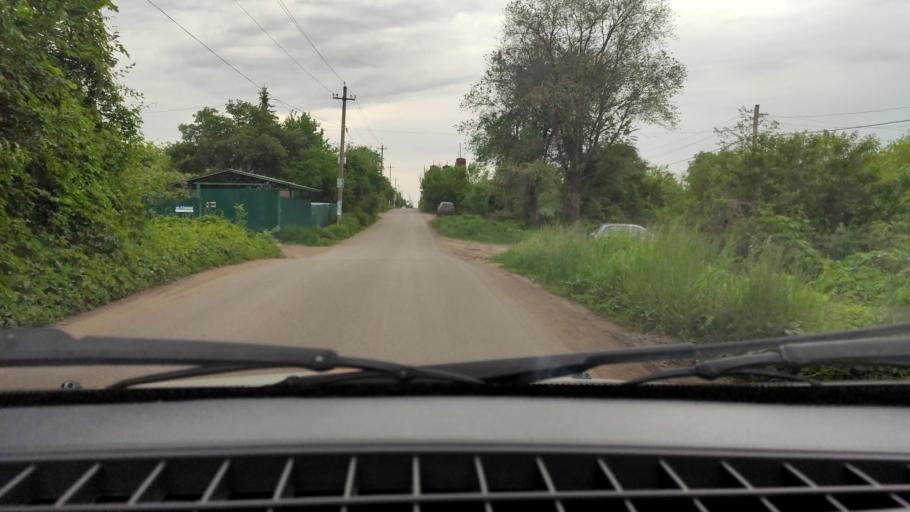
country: RU
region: Voronezj
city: Shilovo
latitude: 51.6020
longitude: 39.1406
